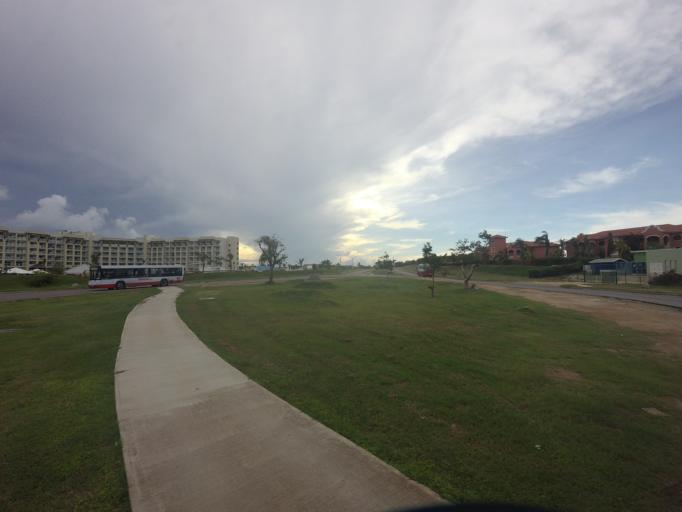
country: CU
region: Matanzas
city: Varadero
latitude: 23.1967
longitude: -81.1278
